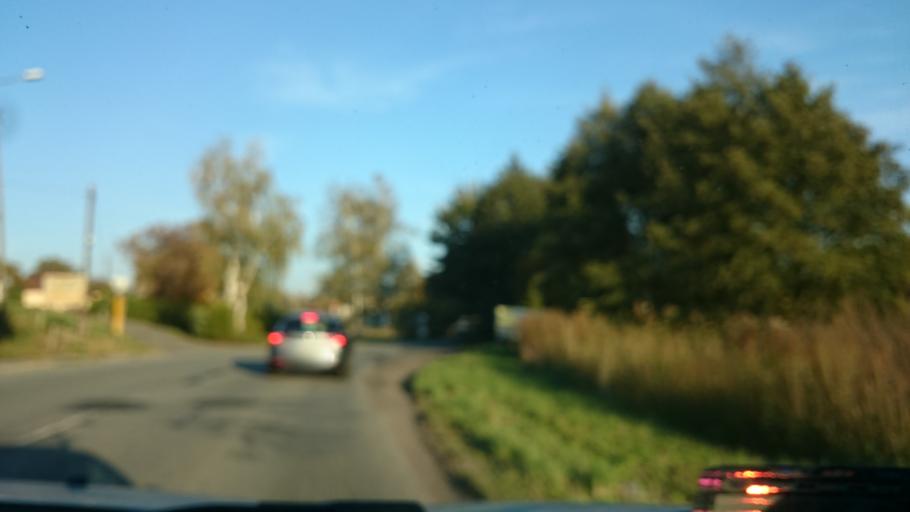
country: PL
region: Silesian Voivodeship
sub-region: Powiat wodzislawski
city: Polomia
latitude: 50.0151
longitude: 18.5512
